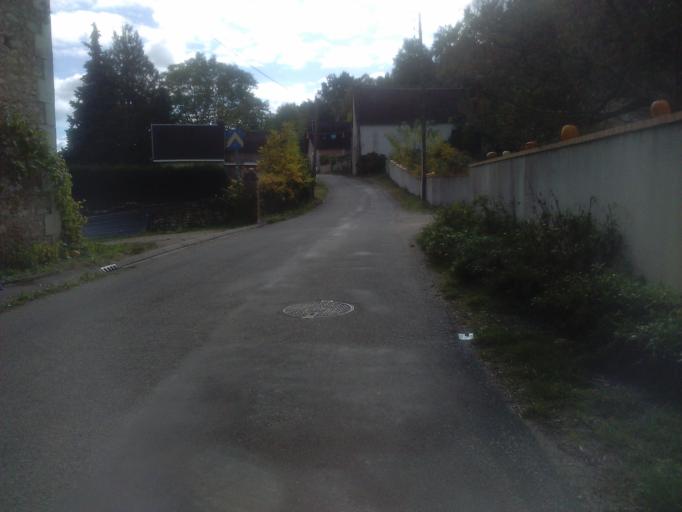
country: FR
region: Centre
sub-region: Departement du Loir-et-Cher
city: Villiers-sur-Loir
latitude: 47.8018
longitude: 0.9789
